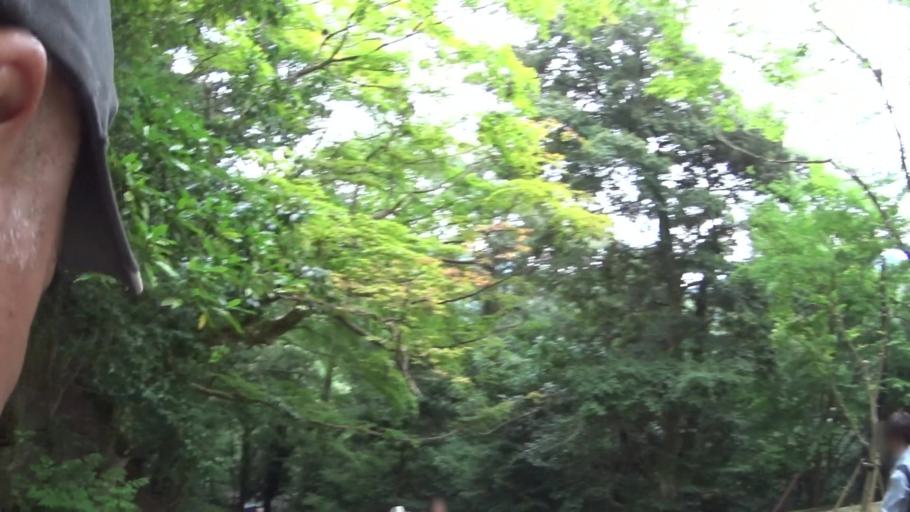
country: JP
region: Kyoto
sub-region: Kyoto-shi
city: Kamigyo-ku
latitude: 35.0548
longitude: 135.6711
